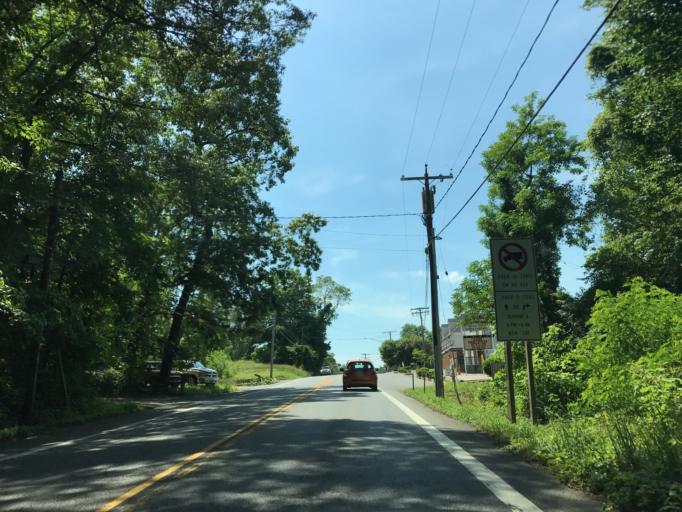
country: US
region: Maryland
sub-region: Anne Arundel County
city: Crofton
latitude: 38.9928
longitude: -76.6688
